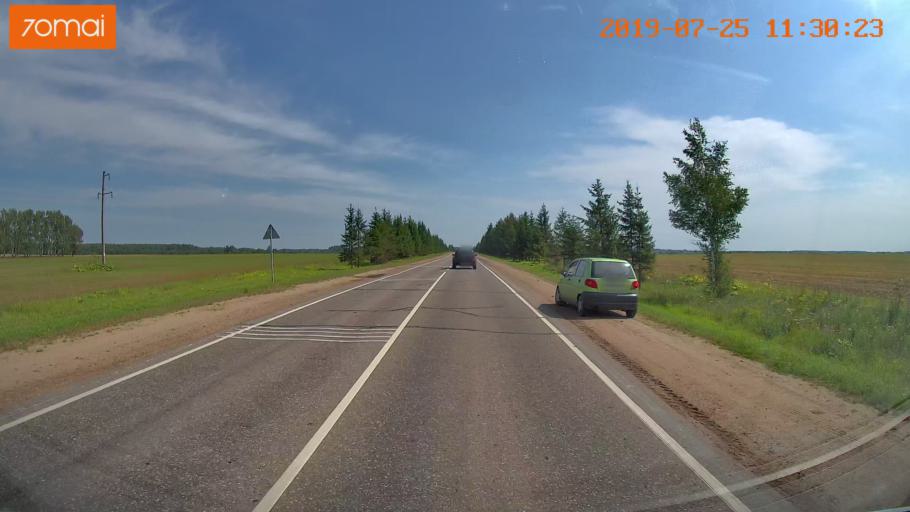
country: RU
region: Ivanovo
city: Privolzhsk
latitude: 57.3868
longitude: 41.3227
